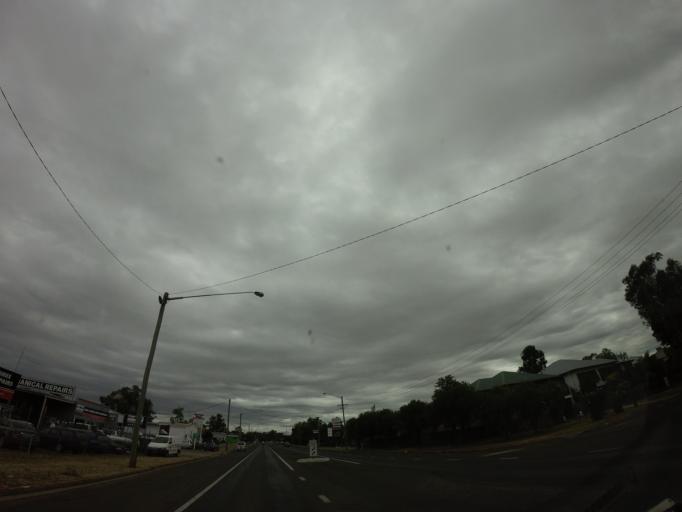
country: AU
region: New South Wales
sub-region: Narrabri
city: Narrabri
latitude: -30.3384
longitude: 149.7674
